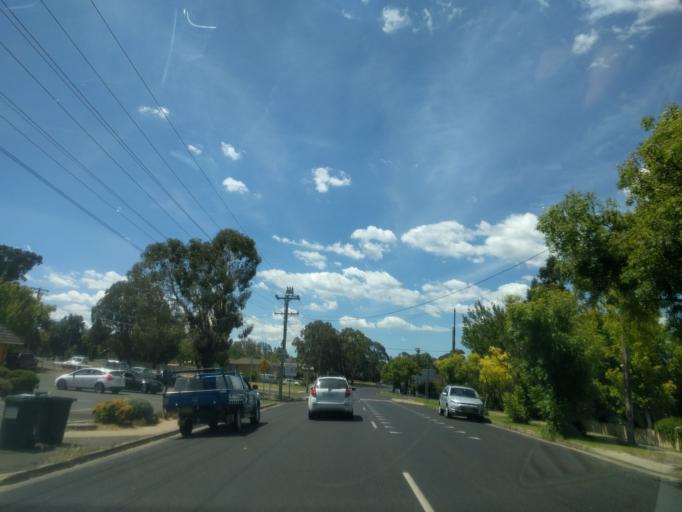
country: AU
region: New South Wales
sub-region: Armidale Dumaresq
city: Armidale
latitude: -30.5009
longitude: 151.6744
